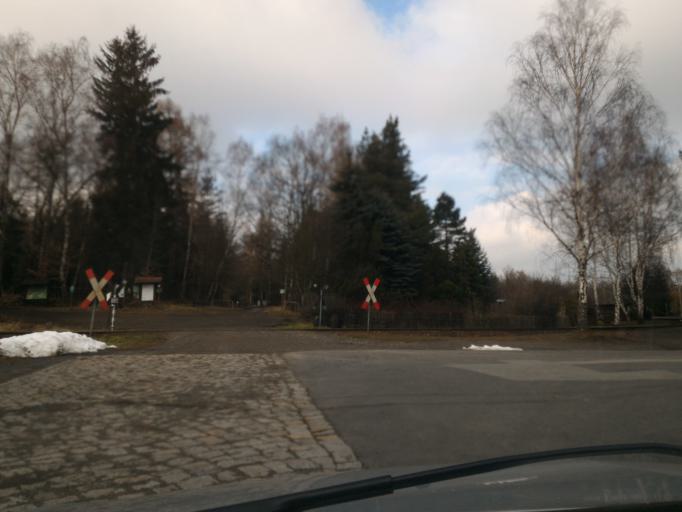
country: DE
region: Saxony
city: Kurort Oybin
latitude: 50.8613
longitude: 14.7543
